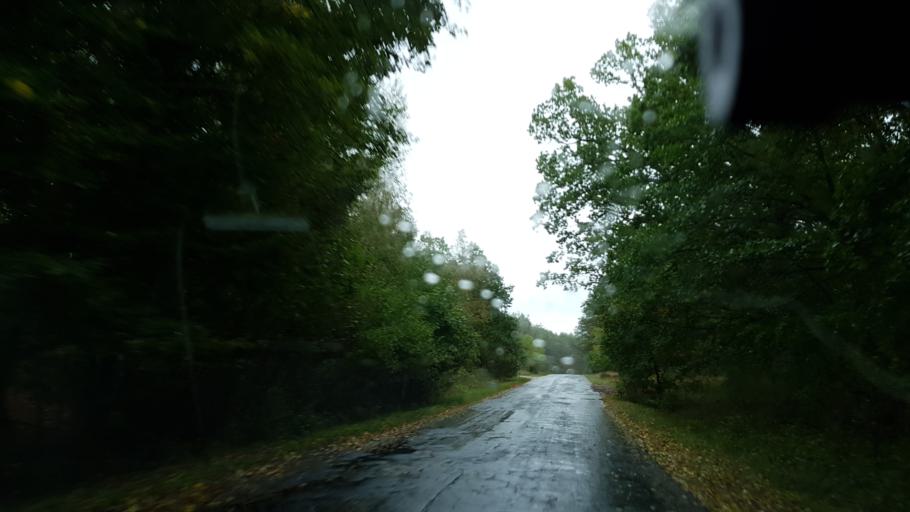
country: PL
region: West Pomeranian Voivodeship
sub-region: Powiat goleniowski
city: Stepnica
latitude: 53.6797
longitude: 14.7183
